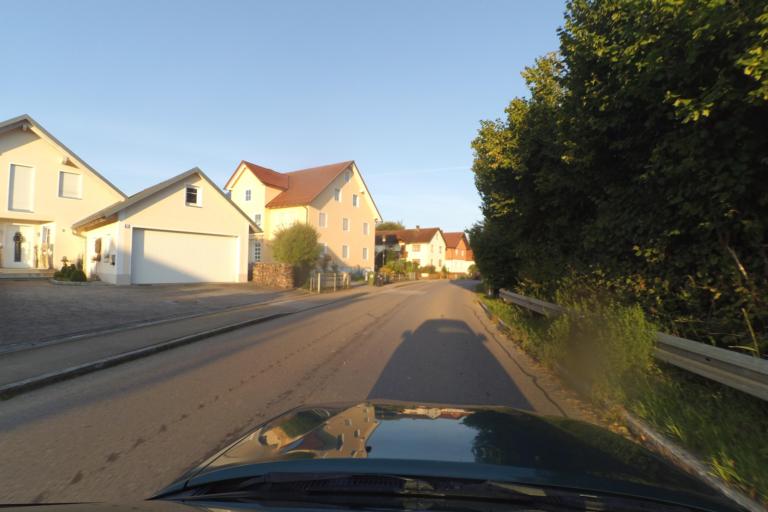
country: DE
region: Bavaria
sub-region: Lower Bavaria
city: Aiglsbach
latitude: 48.6719
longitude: 11.6830
